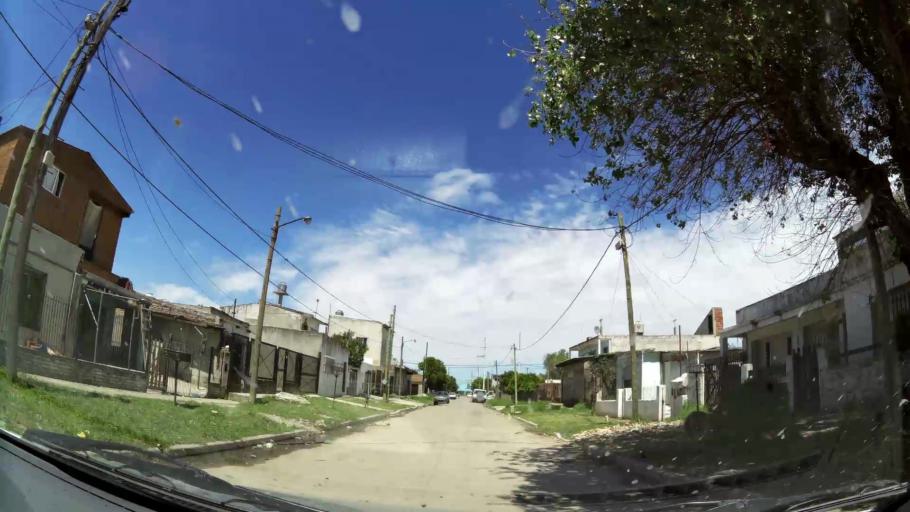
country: AR
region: Buenos Aires
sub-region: Partido de Quilmes
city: Quilmes
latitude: -34.7384
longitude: -58.3133
